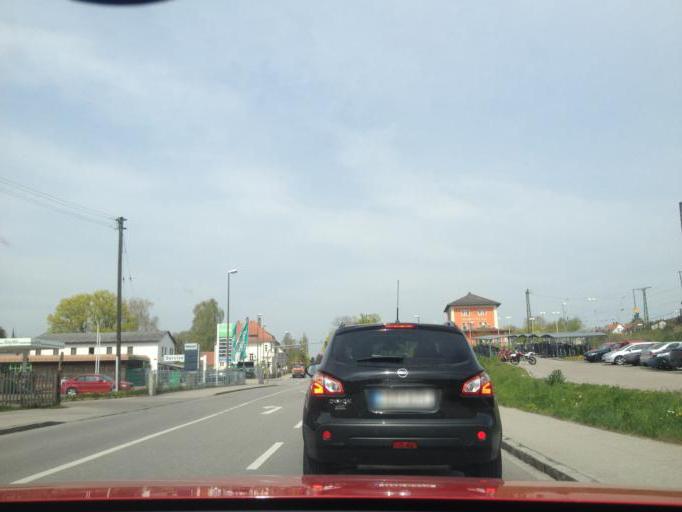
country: DE
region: Bavaria
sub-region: Upper Bavaria
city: Pfaffenhofen an der Ilm
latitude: 48.5214
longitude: 11.5112
